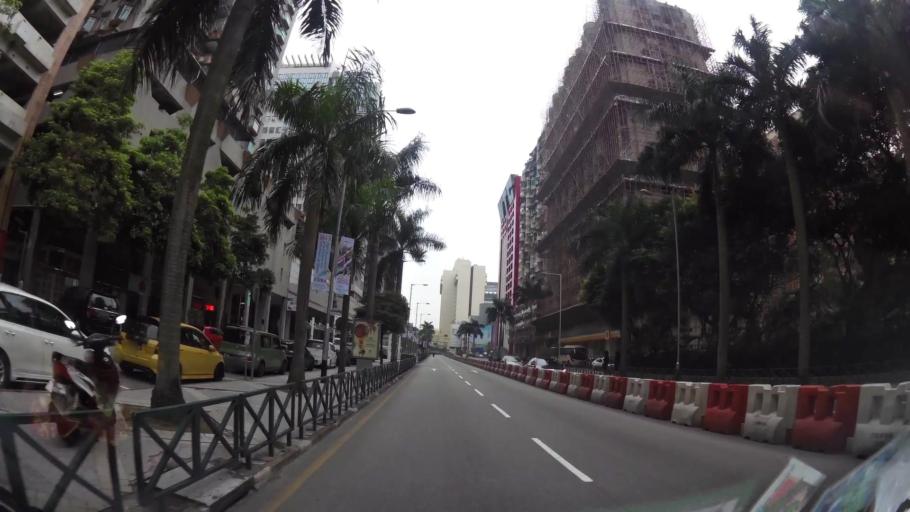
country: MO
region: Macau
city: Macau
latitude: 22.1915
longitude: 113.5504
